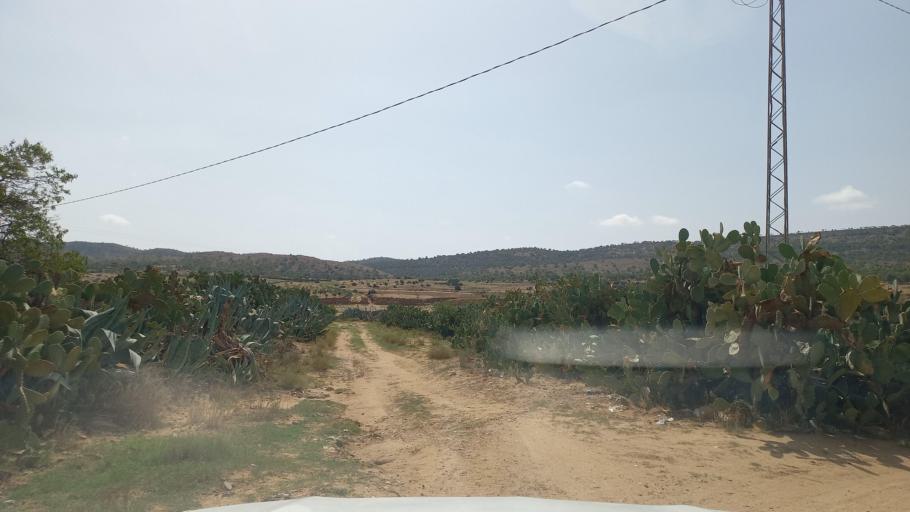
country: TN
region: Al Qasrayn
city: Sbiba
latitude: 35.3857
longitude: 8.9572
